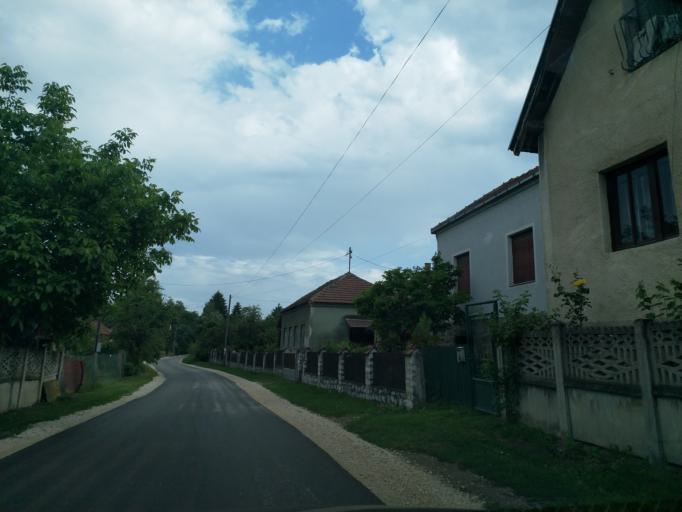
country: RS
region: Central Serbia
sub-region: Borski Okrug
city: Bor
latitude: 44.0140
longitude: 21.9835
